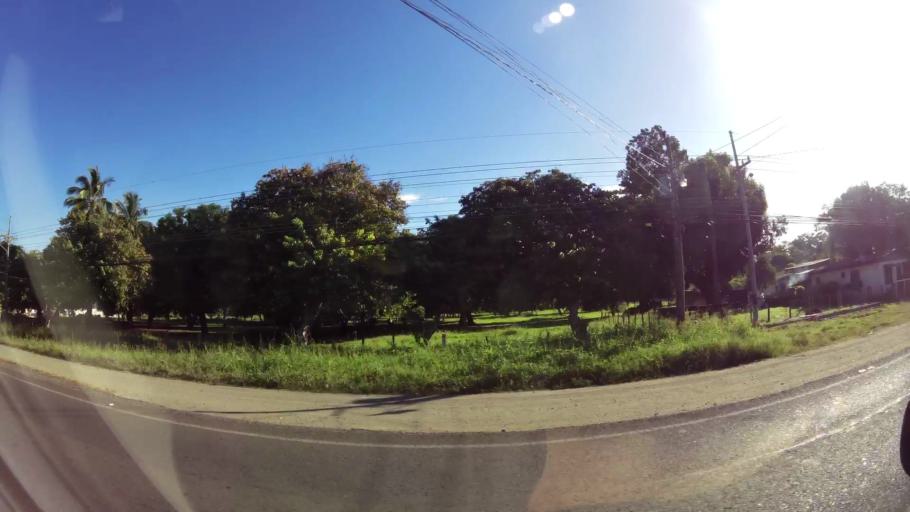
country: CR
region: Guanacaste
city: Belen
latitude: 10.4553
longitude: -85.5559
